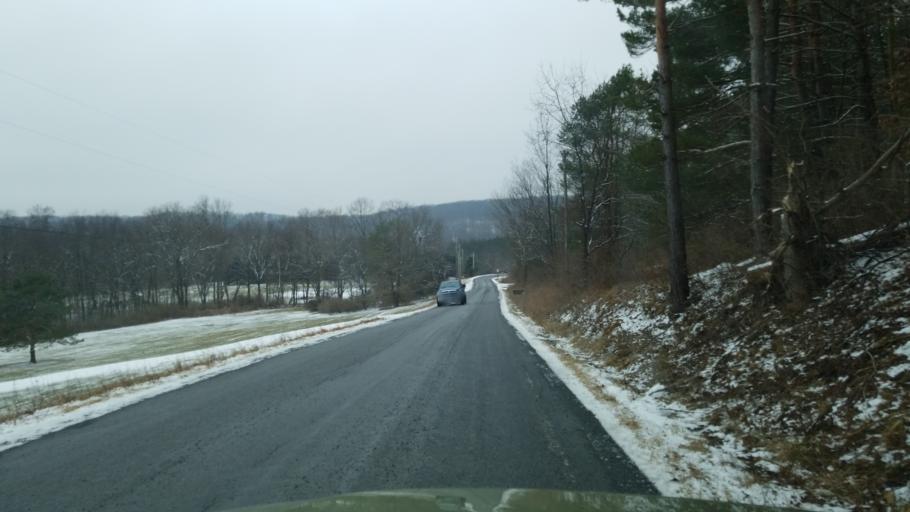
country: US
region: Pennsylvania
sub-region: Jefferson County
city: Sykesville
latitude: 41.0491
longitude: -78.7898
